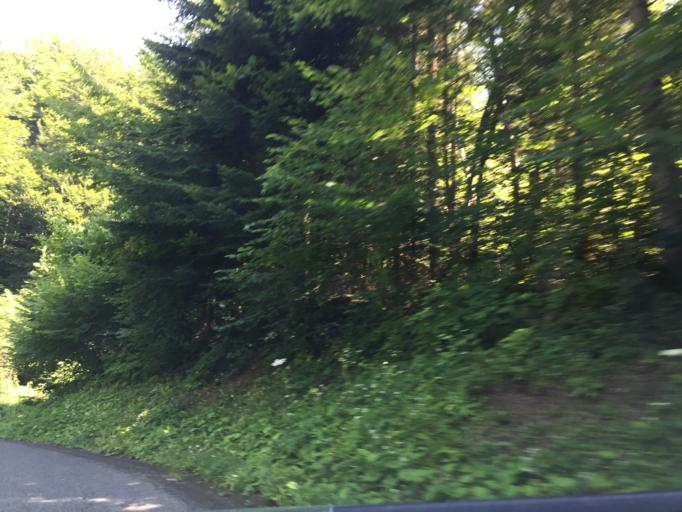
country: SI
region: Prebold
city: Prebold
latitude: 46.1968
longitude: 15.0722
